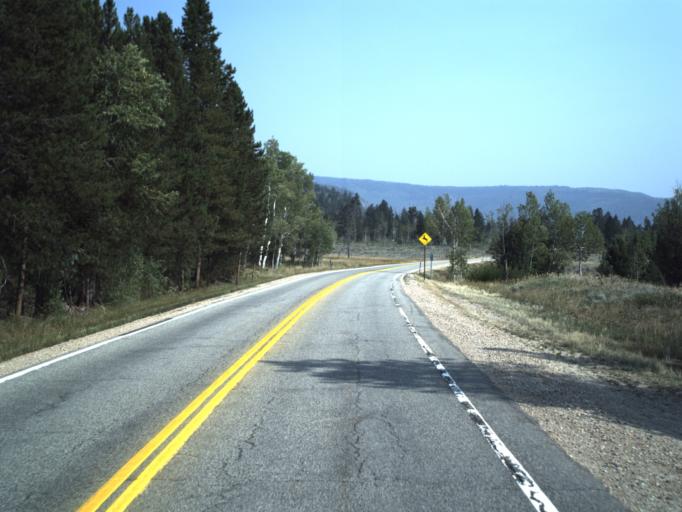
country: US
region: Utah
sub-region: Summit County
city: Francis
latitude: 40.5944
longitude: -111.0743
